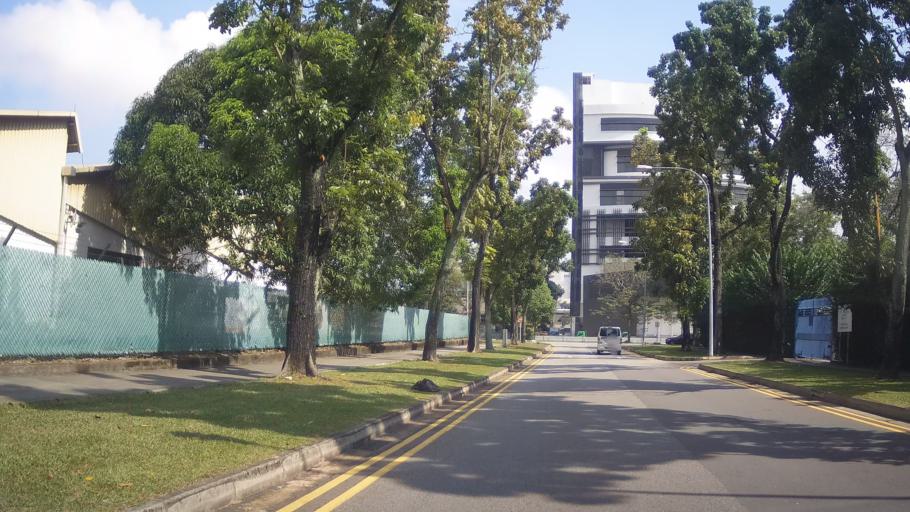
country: MY
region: Johor
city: Johor Bahru
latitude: 1.3268
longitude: 103.7030
